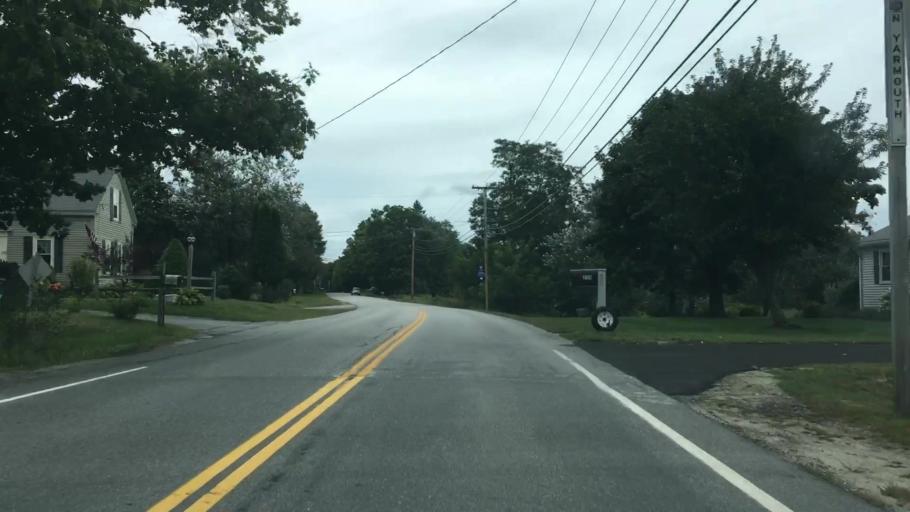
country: US
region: Maine
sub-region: Cumberland County
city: Yarmouth
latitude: 43.8287
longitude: -70.1962
